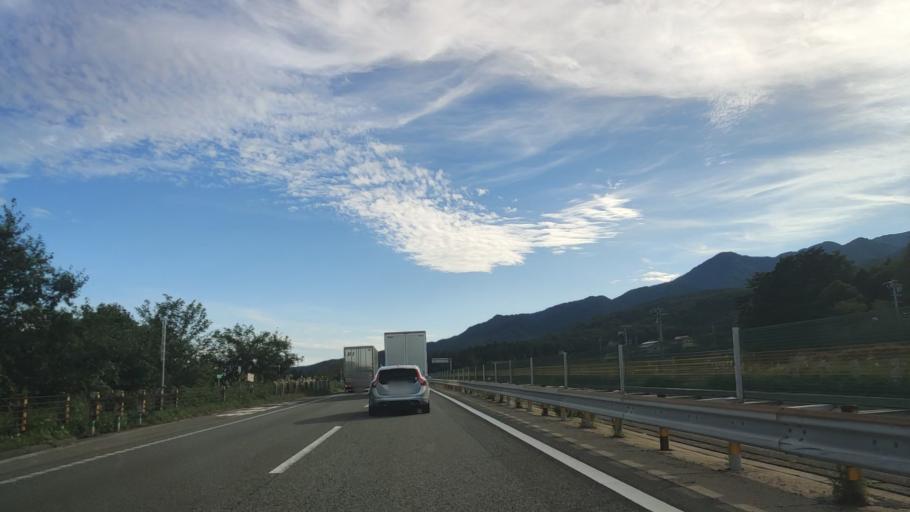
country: JP
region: Nagano
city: Ina
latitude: 35.7234
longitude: 137.9085
